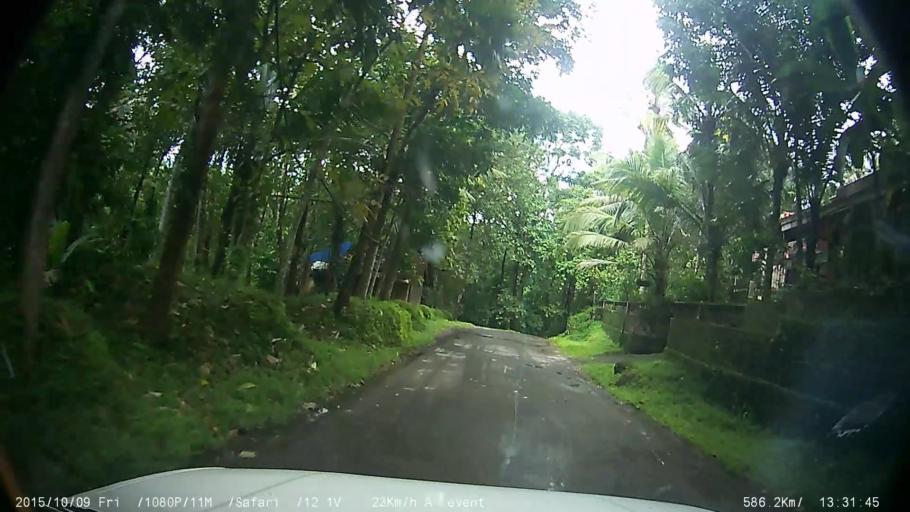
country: IN
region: Kerala
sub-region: Ernakulam
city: Ramamangalam
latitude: 9.9125
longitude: 76.5568
